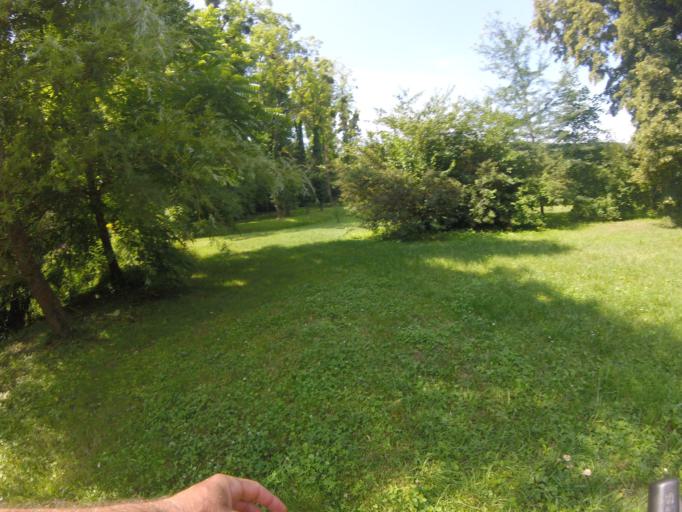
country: HU
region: Zala
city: Letenye
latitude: 46.5095
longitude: 16.7009
